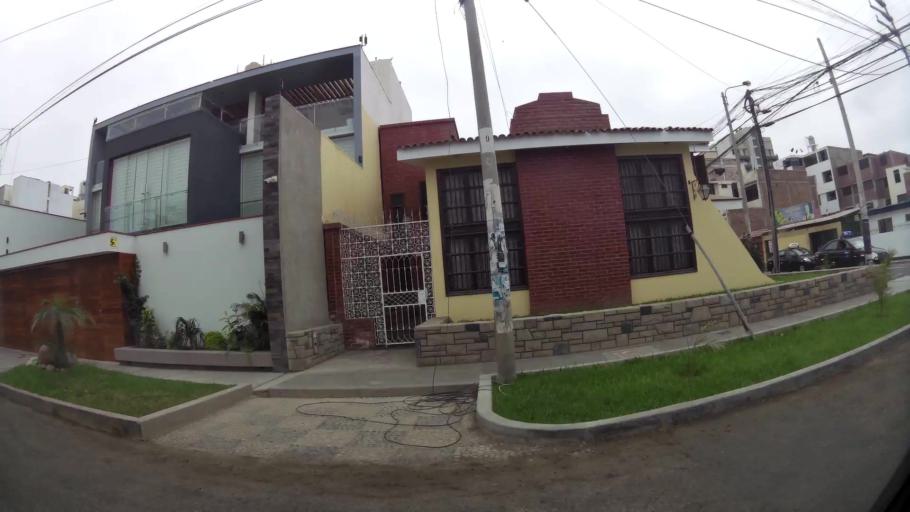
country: PE
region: La Libertad
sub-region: Provincia de Trujillo
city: Buenos Aires
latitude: -8.1307
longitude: -79.0408
